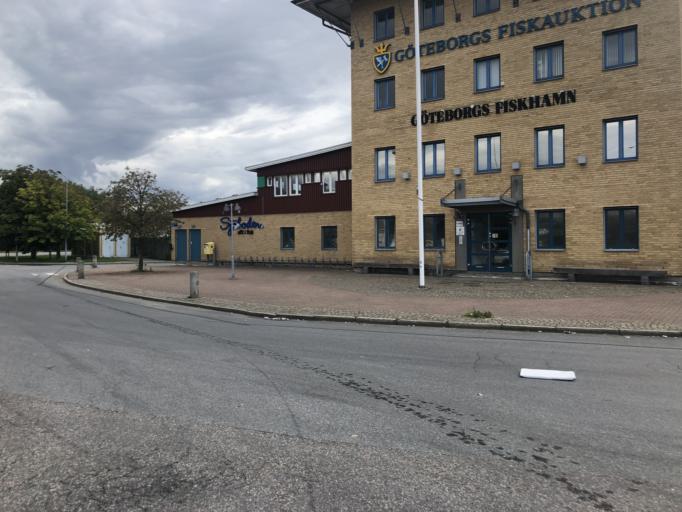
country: SE
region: Vaestra Goetaland
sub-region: Goteborg
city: Majorna
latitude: 57.6997
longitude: 11.9286
